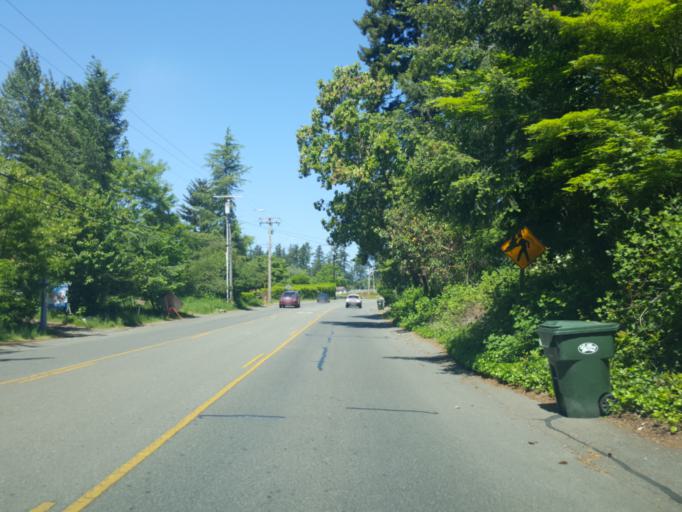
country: US
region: Washington
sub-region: Pierce County
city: Steilacoom
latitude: 47.1566
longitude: -122.5751
